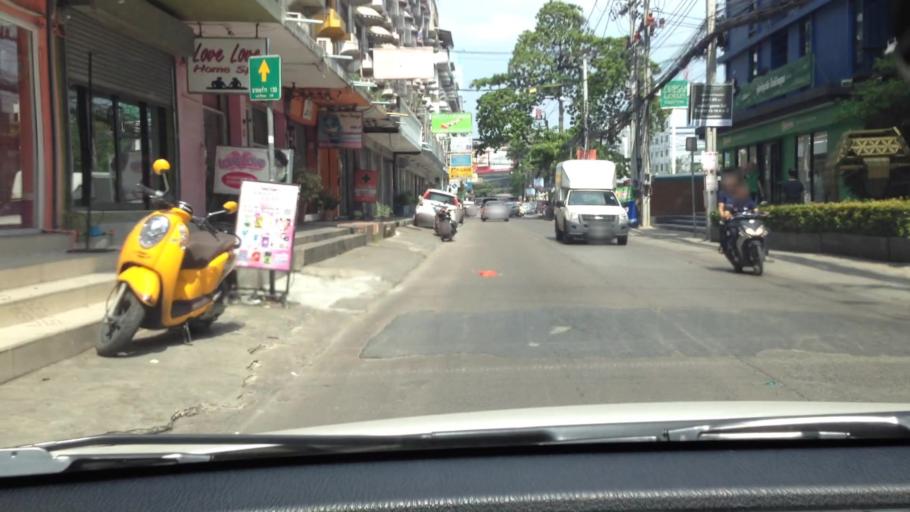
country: TH
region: Bangkok
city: Bang Kapi
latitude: 13.7716
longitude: 100.6320
